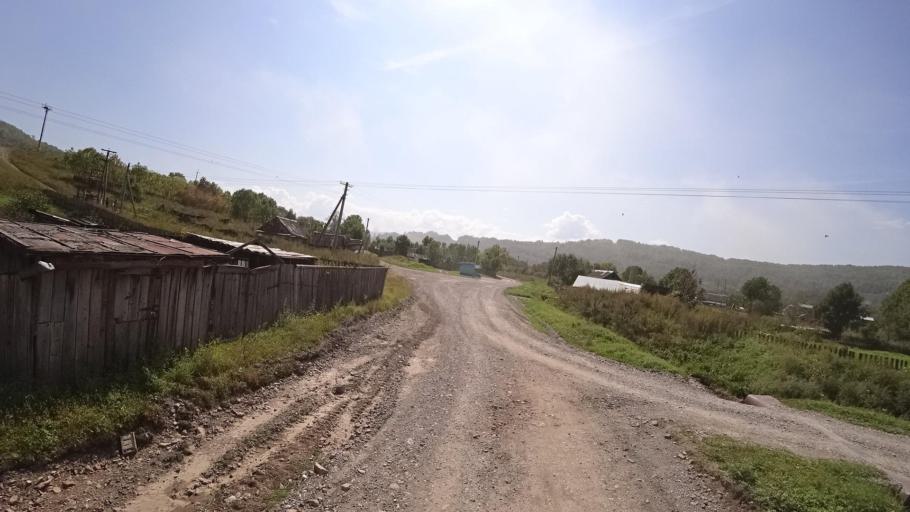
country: RU
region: Jewish Autonomous Oblast
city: Londoko
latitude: 49.0265
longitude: 131.9323
